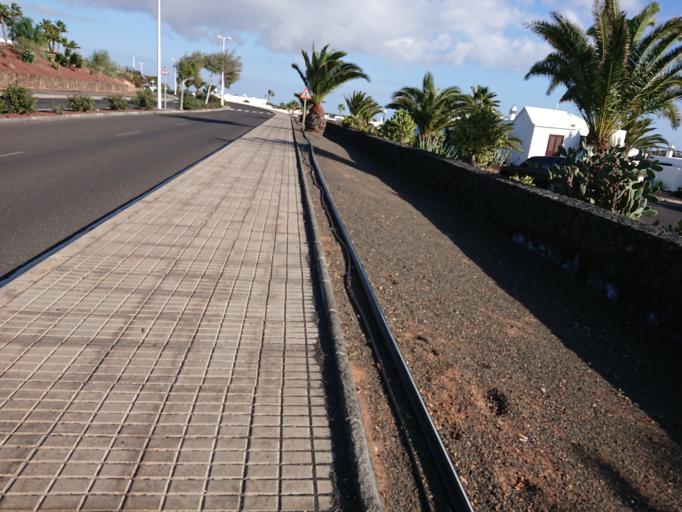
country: ES
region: Canary Islands
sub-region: Provincia de Las Palmas
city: Playa Blanca
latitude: 28.8651
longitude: -13.8468
